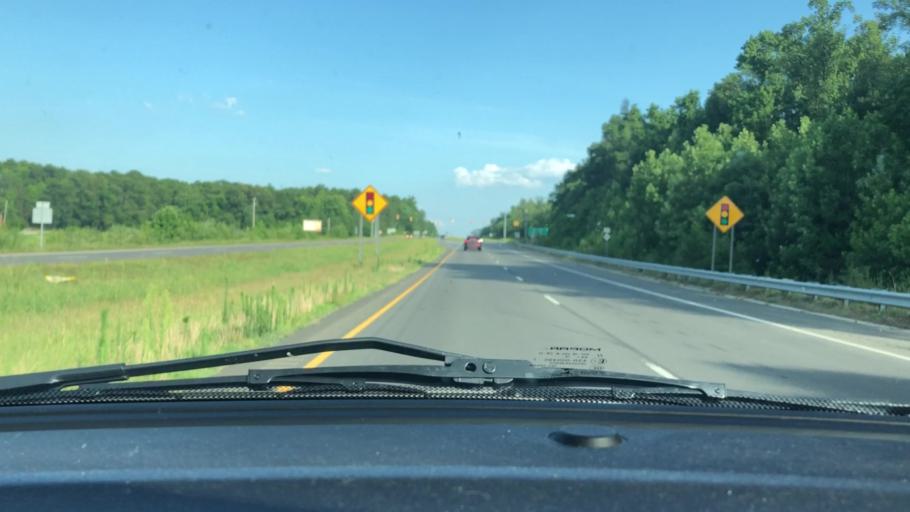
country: US
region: North Carolina
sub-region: Chatham County
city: Siler City
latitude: 35.6332
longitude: -79.3706
